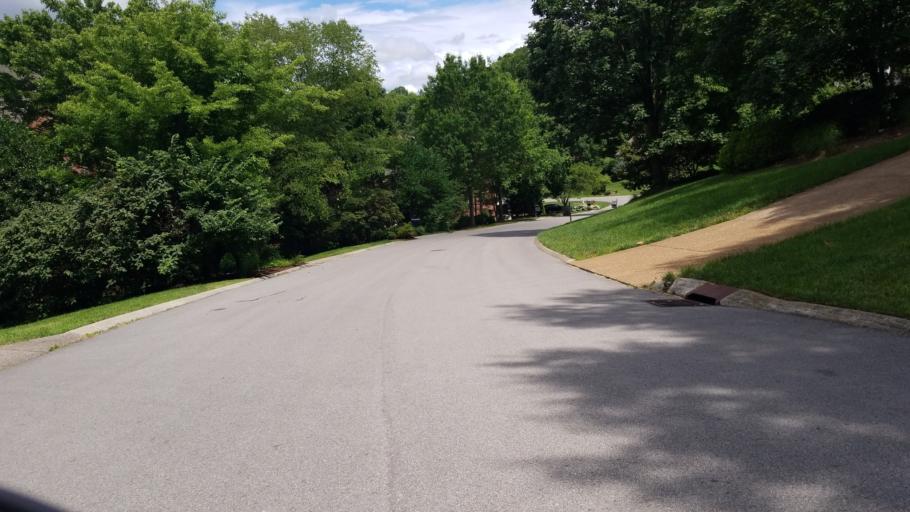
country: US
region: Tennessee
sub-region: Davidson County
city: Forest Hills
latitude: 36.0293
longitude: -86.8411
